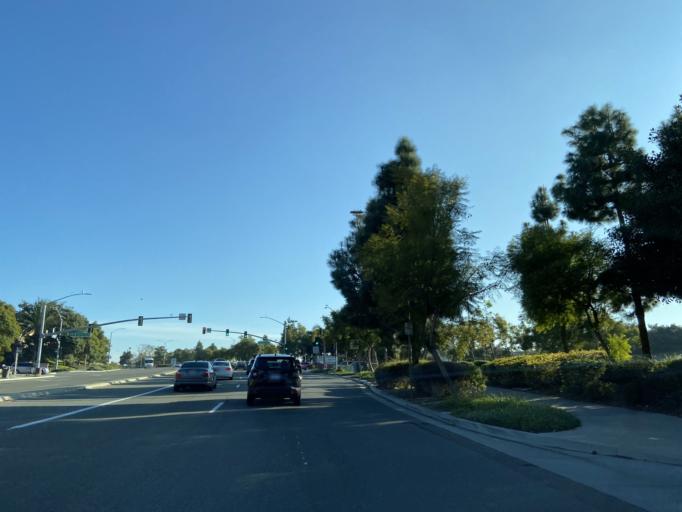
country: US
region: California
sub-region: San Diego County
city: Bonita
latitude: 32.6339
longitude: -116.9675
